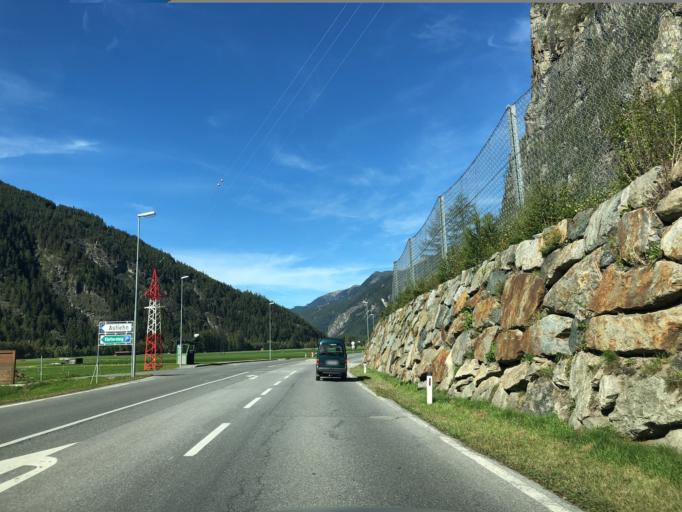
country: AT
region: Tyrol
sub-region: Politischer Bezirk Imst
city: Umhausen
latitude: 47.0574
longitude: 10.9651
